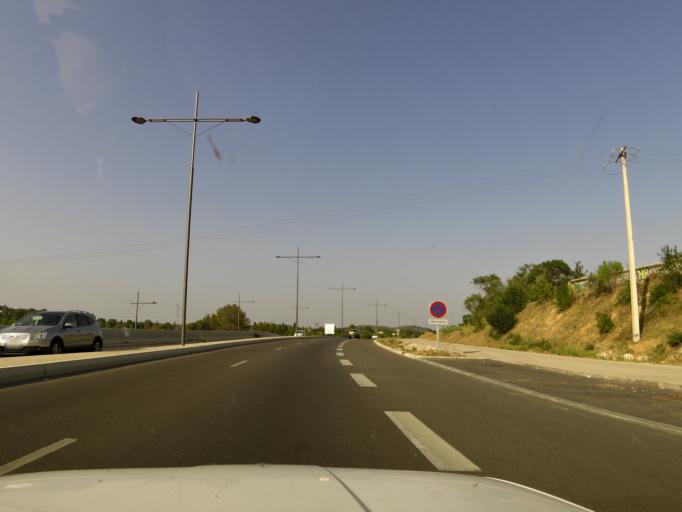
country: FR
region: Languedoc-Roussillon
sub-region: Departement de l'Herault
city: Montferrier-sur-Lez
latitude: 43.6491
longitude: 3.8560
